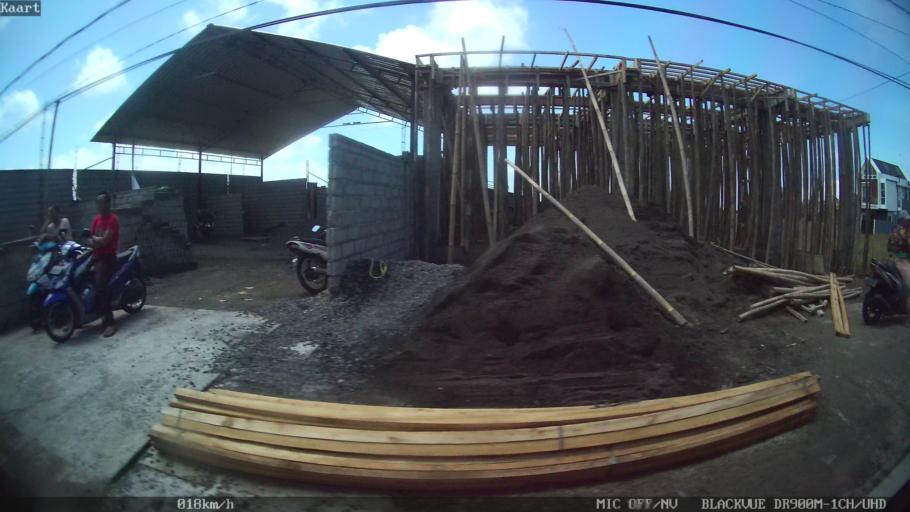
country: ID
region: Bali
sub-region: Kabupaten Gianyar
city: Ubud
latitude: -8.5608
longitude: 115.3187
